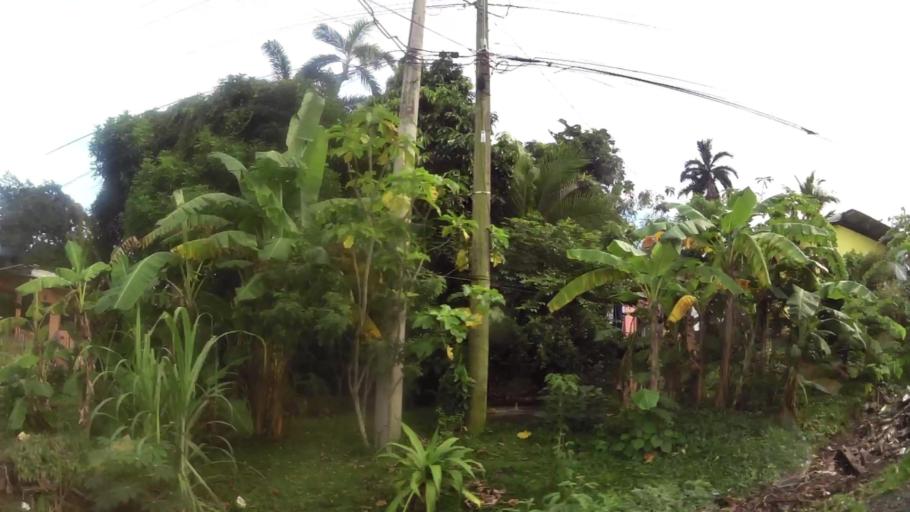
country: PA
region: Panama
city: El Coco
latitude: 8.8712
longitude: -79.8057
